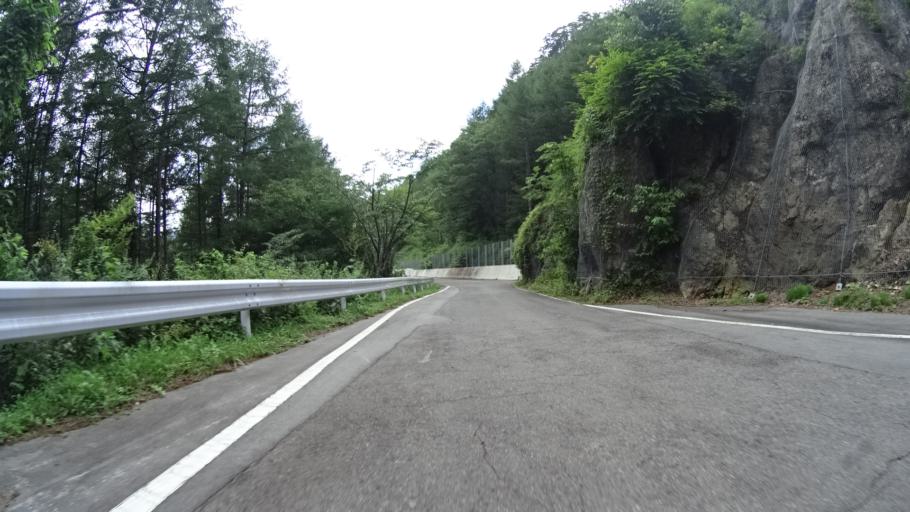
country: JP
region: Nagano
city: Saku
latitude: 36.0693
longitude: 138.6378
